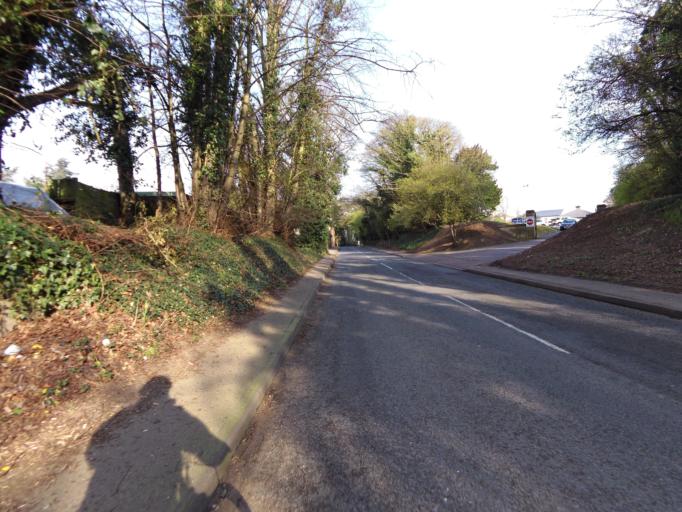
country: GB
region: England
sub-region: Suffolk
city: Bramford
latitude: 52.0712
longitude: 1.1094
